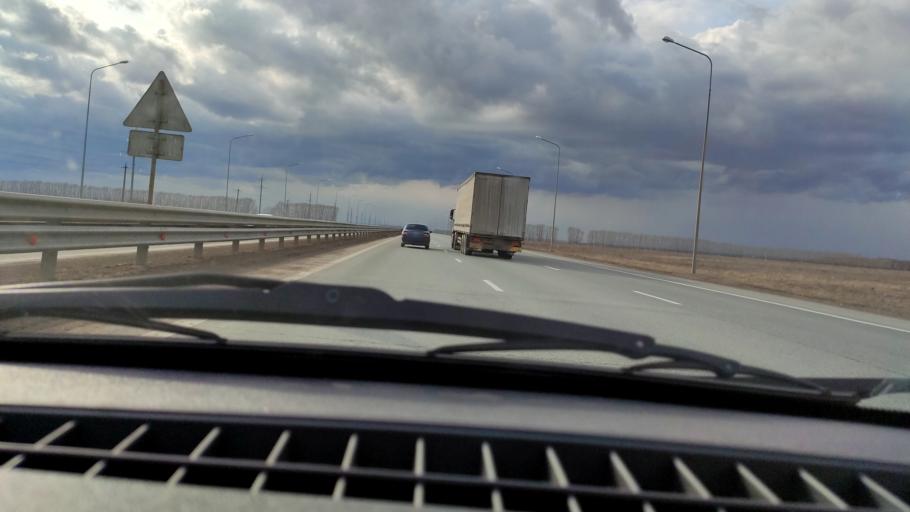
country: RU
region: Bashkortostan
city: Asanovo
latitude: 54.8862
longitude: 55.6709
